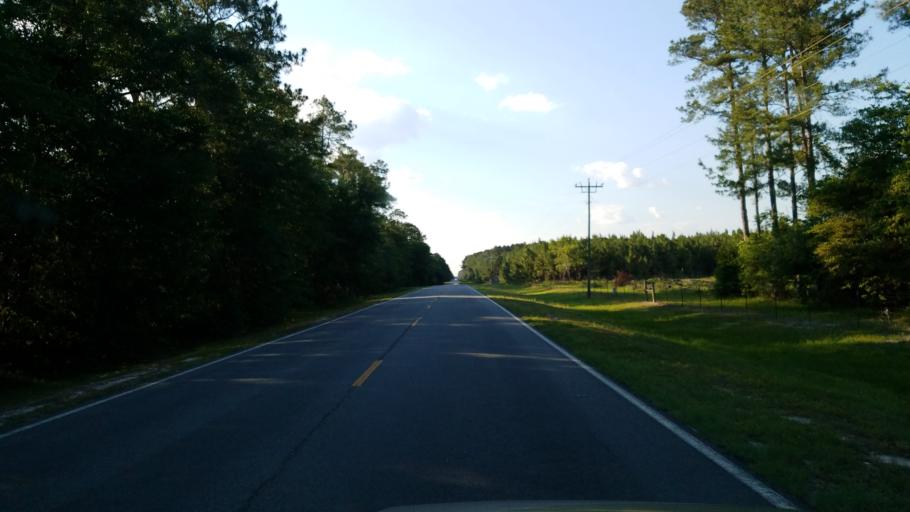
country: US
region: Georgia
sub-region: Lanier County
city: Lakeland
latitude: 31.0668
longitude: -83.0723
